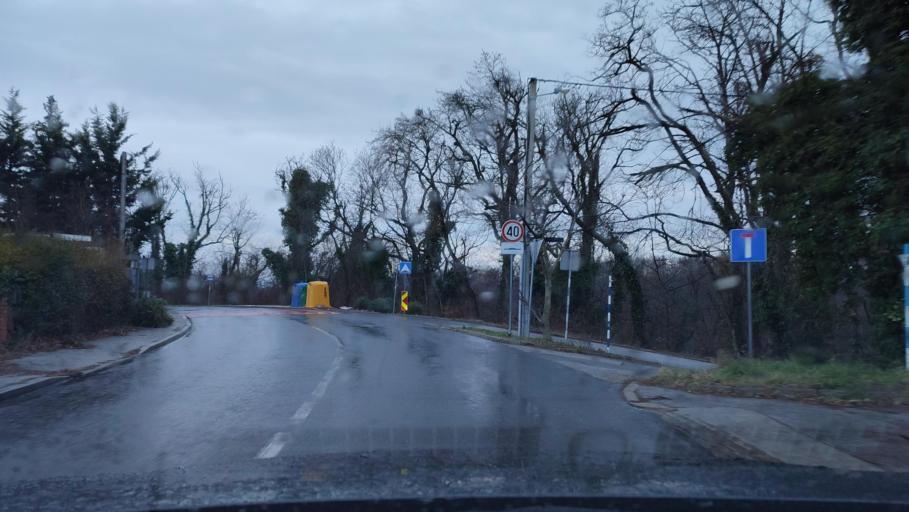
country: HR
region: Grad Zagreb
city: Zagreb
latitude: 45.8406
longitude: 15.9690
